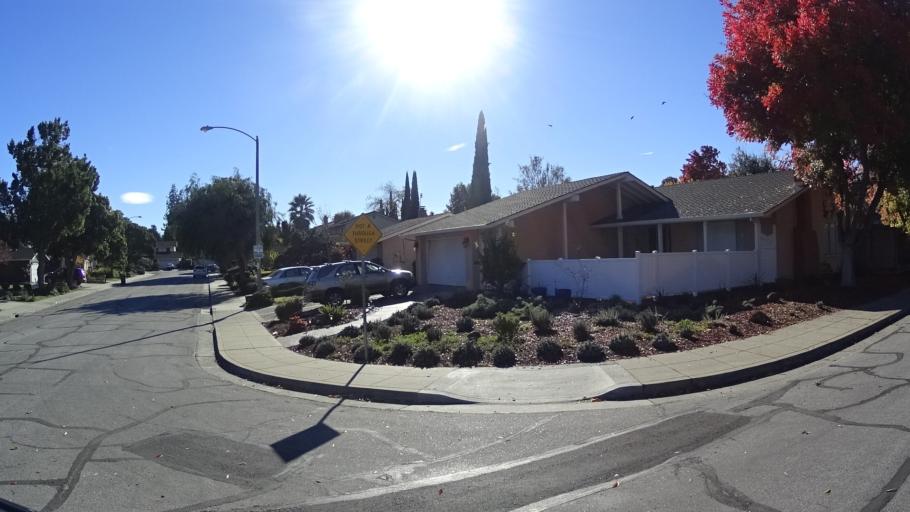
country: US
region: California
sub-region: Santa Clara County
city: Cupertino
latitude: 37.3448
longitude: -122.0247
